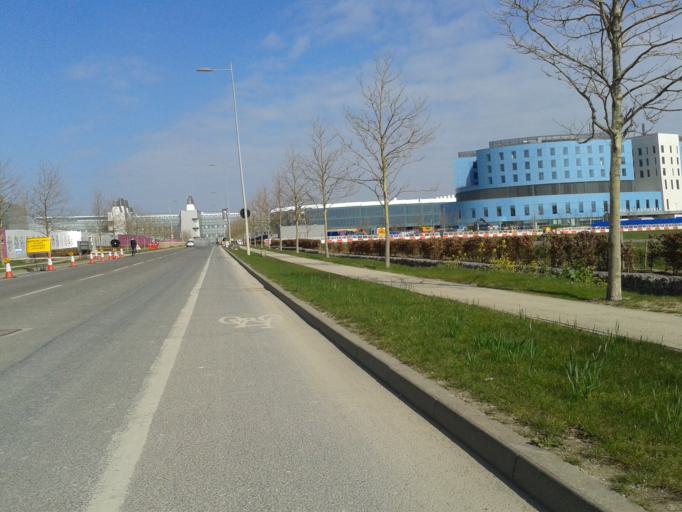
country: GB
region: England
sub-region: Cambridgeshire
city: Cambridge
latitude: 52.1711
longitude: 0.1339
